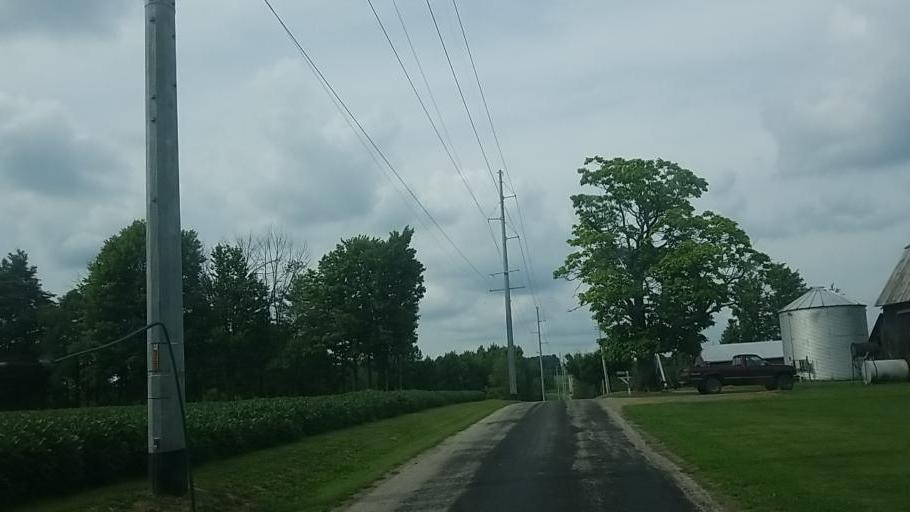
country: US
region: Ohio
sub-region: Sandusky County
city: Bellville
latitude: 40.5603
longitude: -82.5475
